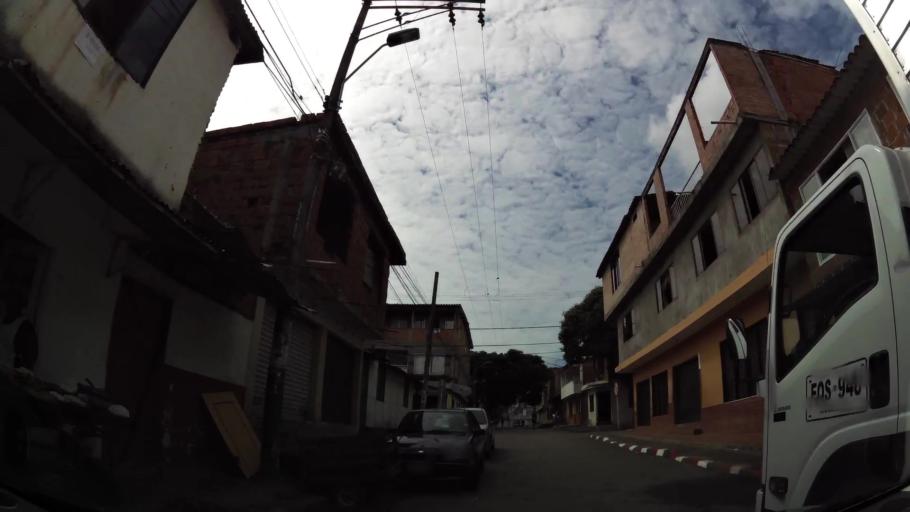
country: CO
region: Valle del Cauca
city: Cali
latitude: 3.3878
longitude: -76.5550
